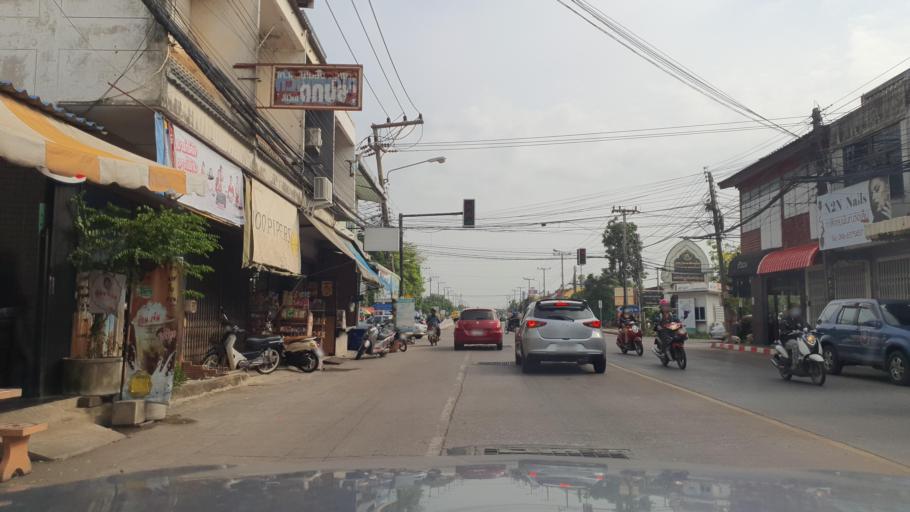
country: TH
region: Phitsanulok
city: Phitsanulok
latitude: 16.8382
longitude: 100.2656
